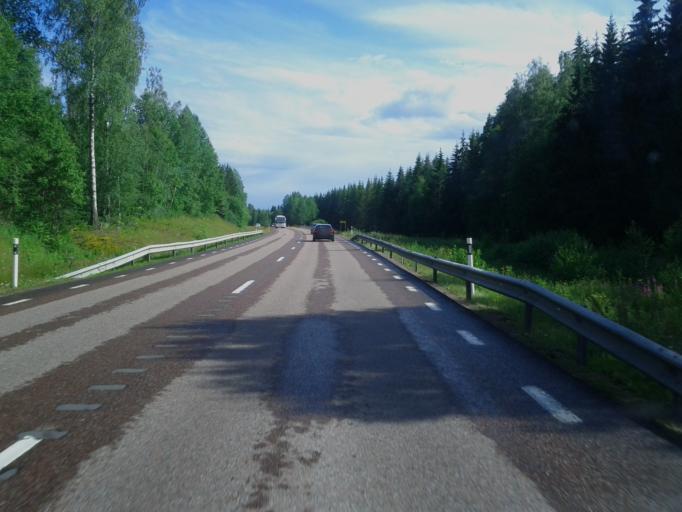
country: SE
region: Dalarna
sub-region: Faluns Kommun
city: Falun
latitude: 60.6537
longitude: 15.5568
